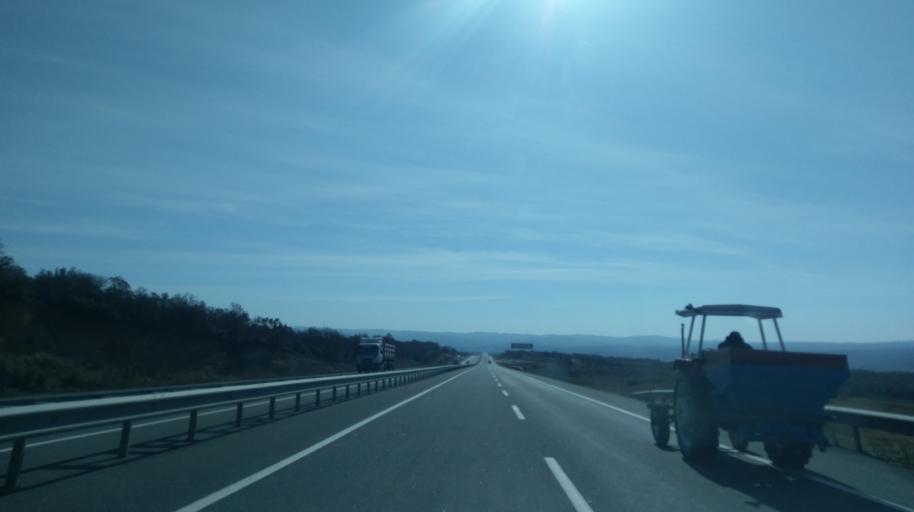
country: TR
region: Edirne
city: Kesan
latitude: 40.8087
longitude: 26.6589
